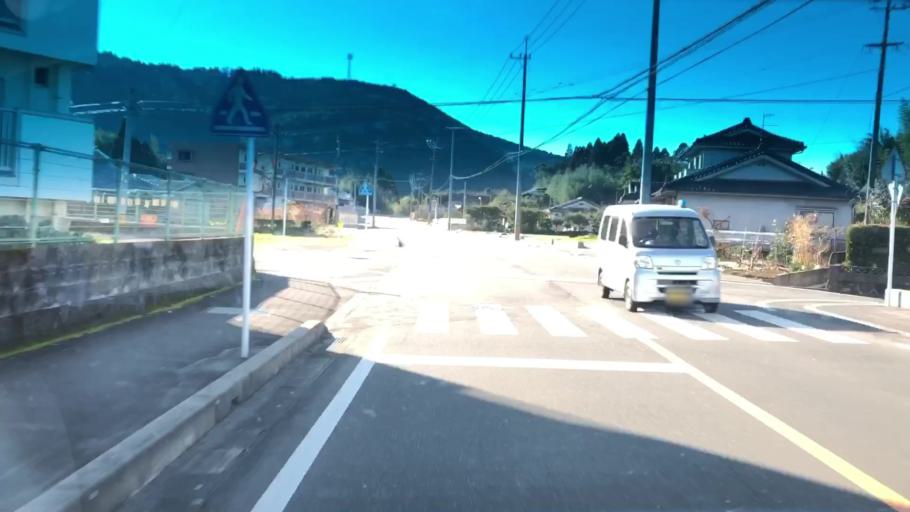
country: JP
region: Kagoshima
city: Satsumasendai
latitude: 31.8167
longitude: 130.2753
